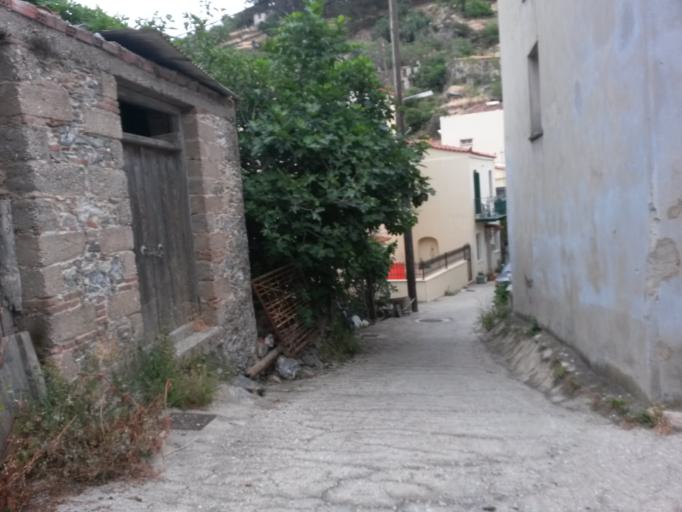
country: GR
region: North Aegean
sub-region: Nomos Lesvou
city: Plomarion
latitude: 38.9780
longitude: 26.3702
